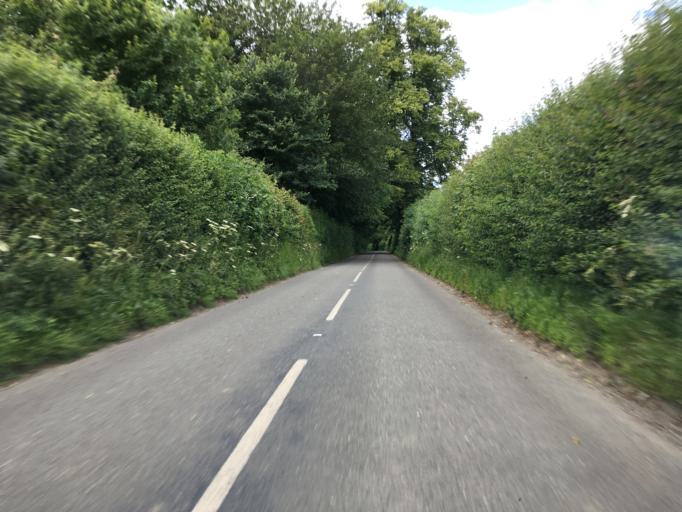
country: GB
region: England
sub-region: West Berkshire
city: Welford
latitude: 51.4594
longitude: -1.4161
